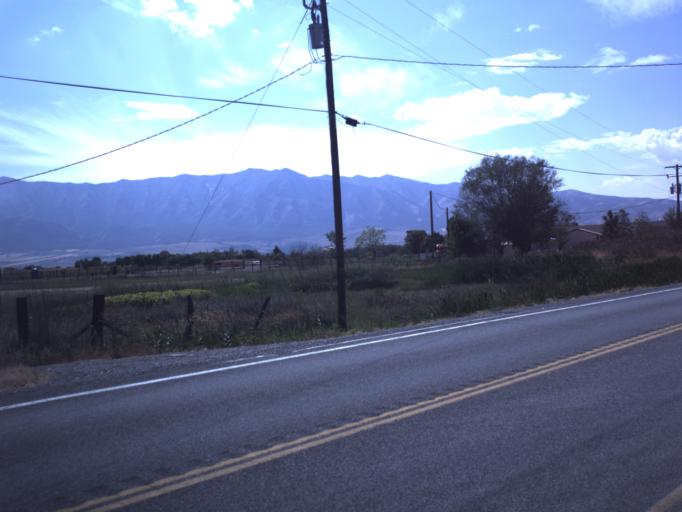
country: US
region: Utah
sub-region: Cache County
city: Logan
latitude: 41.7363
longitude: -111.8893
